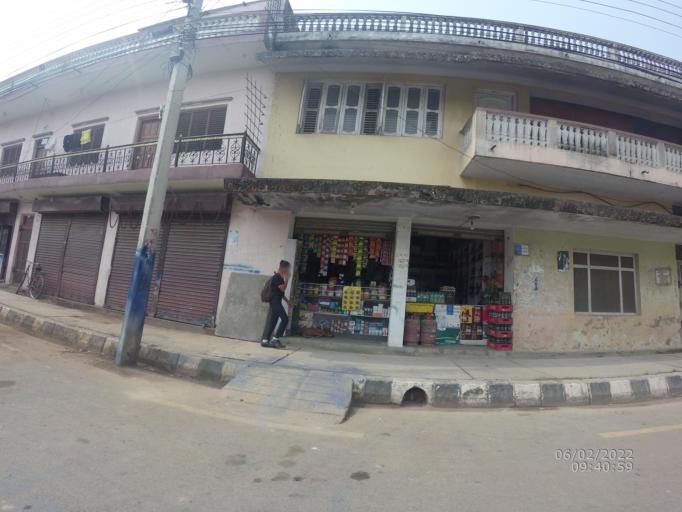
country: NP
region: Western Region
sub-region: Lumbini Zone
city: Bhairahawa
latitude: 27.5019
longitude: 83.4551
